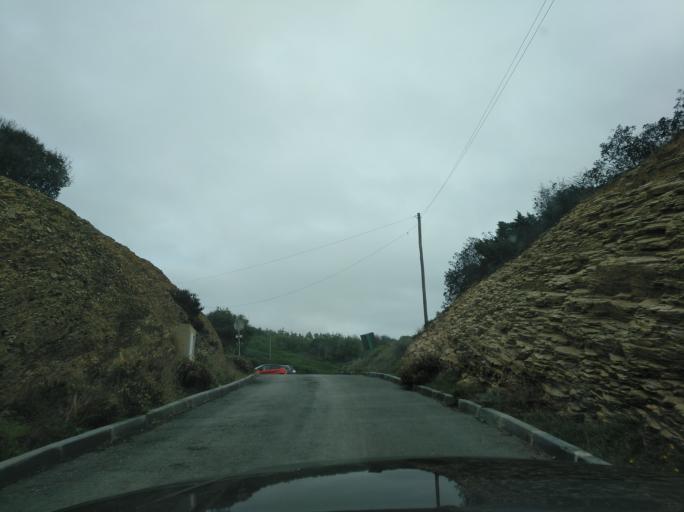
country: PT
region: Beja
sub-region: Odemira
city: Sao Teotonio
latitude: 37.5515
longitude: -8.7915
